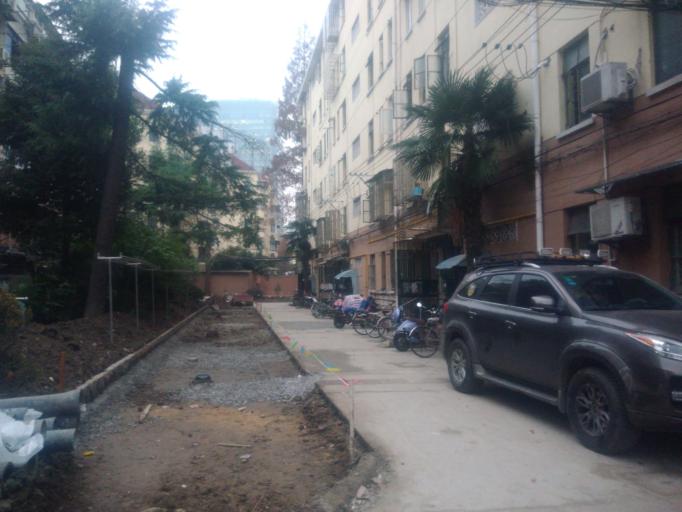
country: CN
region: Shanghai Shi
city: Changning
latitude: 31.2105
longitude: 121.3939
